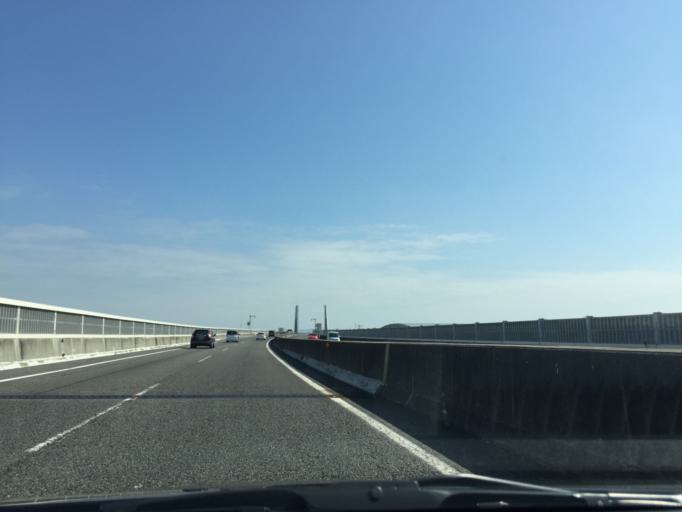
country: JP
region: Aichi
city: Kuroda
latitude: 35.3549
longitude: 136.7953
